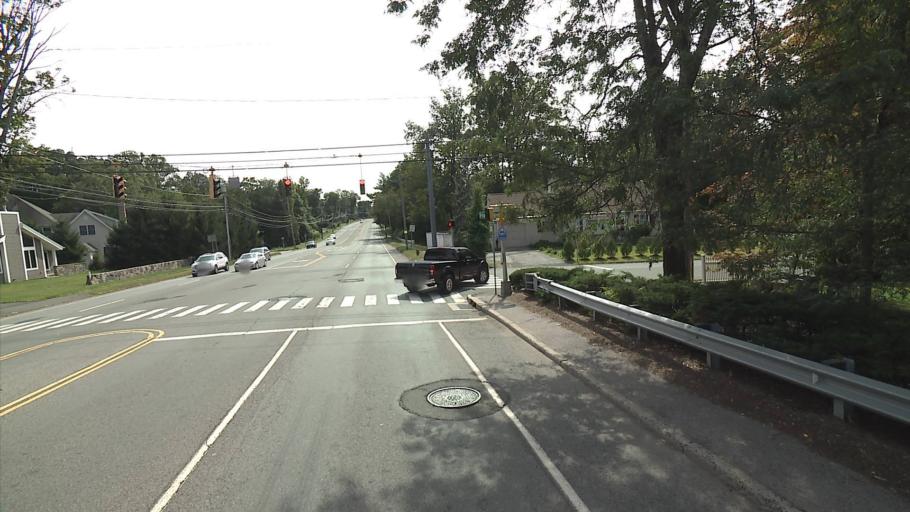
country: US
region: Connecticut
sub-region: Fairfield County
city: North Stamford
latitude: 41.0967
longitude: -73.5478
